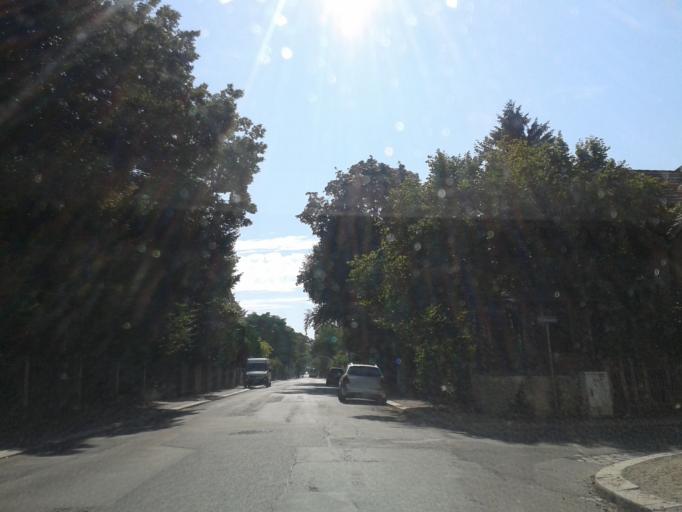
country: DE
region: Saxony
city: Albertstadt
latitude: 51.0509
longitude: 13.8040
